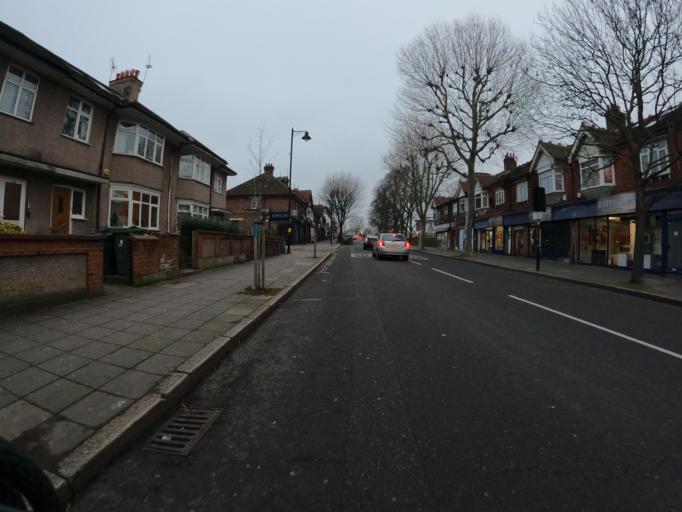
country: GB
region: England
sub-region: Greater London
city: Brentford
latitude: 51.4981
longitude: -0.3136
